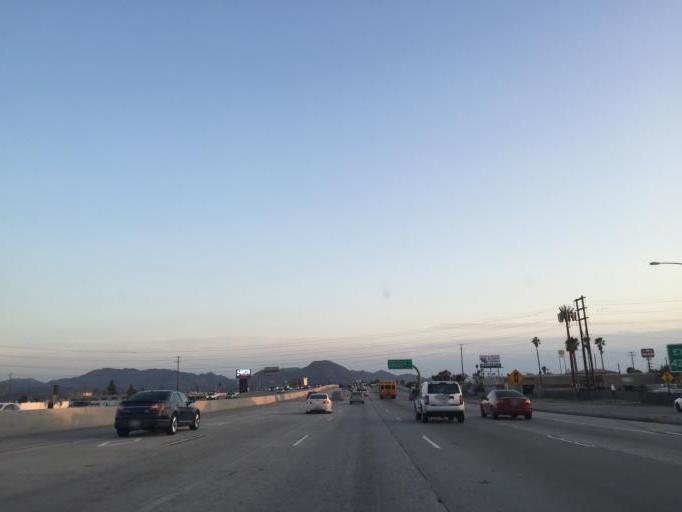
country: US
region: California
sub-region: San Bernardino County
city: San Bernardino
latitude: 34.0951
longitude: -117.3020
